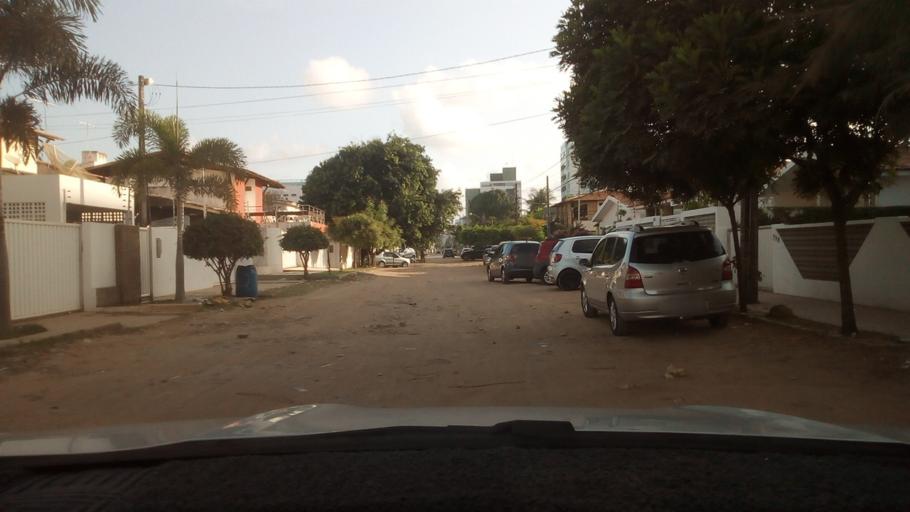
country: BR
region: Paraiba
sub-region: Cabedelo
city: Cabedelo
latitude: -7.0119
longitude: -34.8284
